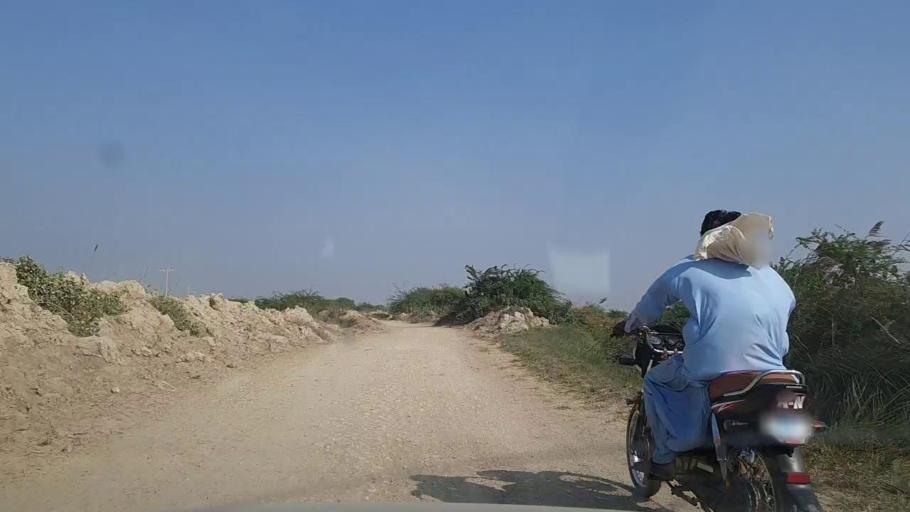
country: PK
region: Sindh
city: Mirpur Sakro
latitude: 24.5544
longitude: 67.5741
